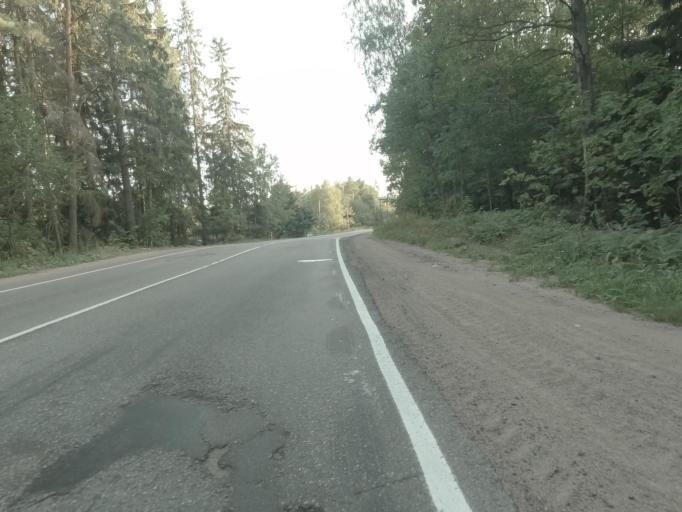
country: RU
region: Leningrad
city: Vyborg
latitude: 60.7435
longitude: 28.7682
